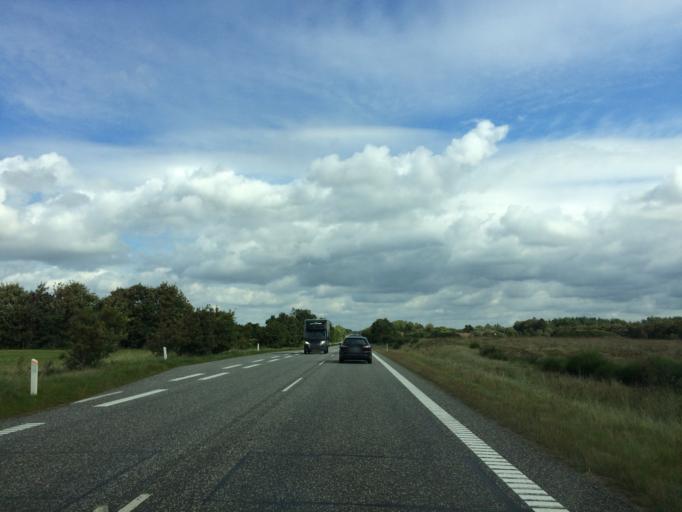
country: DK
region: Central Jutland
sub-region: Holstebro Kommune
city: Vinderup
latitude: 56.3806
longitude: 8.7688
